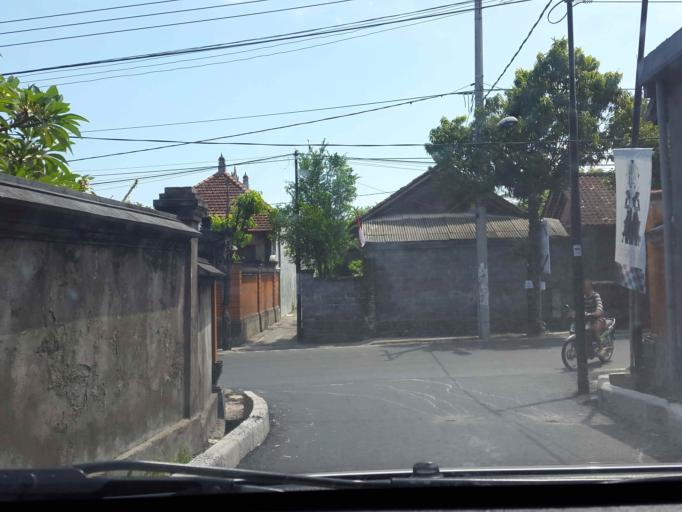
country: ID
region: Bali
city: Semarapura
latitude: -8.5497
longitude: 115.4030
